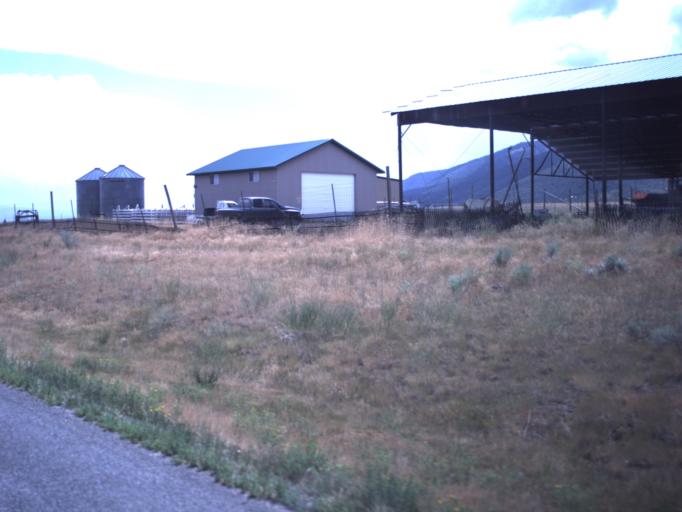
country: US
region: Utah
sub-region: Sanpete County
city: Fountain Green
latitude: 39.6774
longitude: -111.6689
